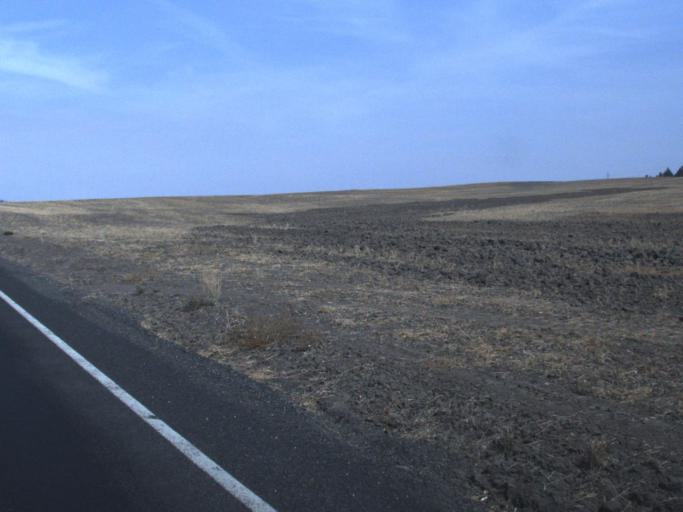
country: US
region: Idaho
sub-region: Benewah County
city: Plummer
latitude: 47.2633
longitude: -117.1310
